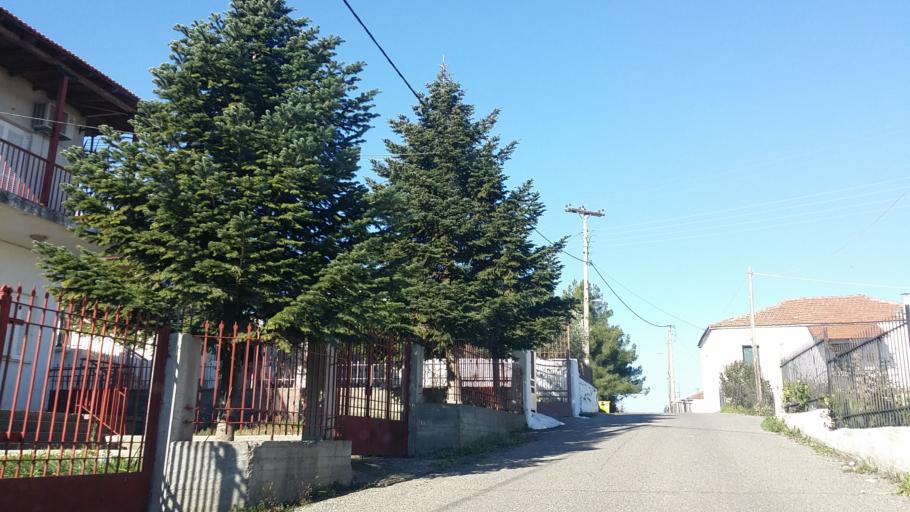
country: GR
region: West Greece
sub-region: Nomos Aitolias kai Akarnanias
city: Fitiai
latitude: 38.7090
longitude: 21.1753
